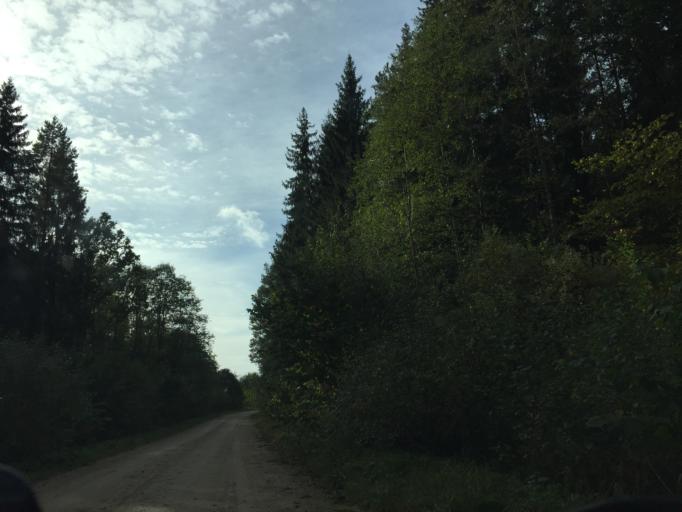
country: LV
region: Jaunpils
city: Jaunpils
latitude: 56.6121
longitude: 23.0146
